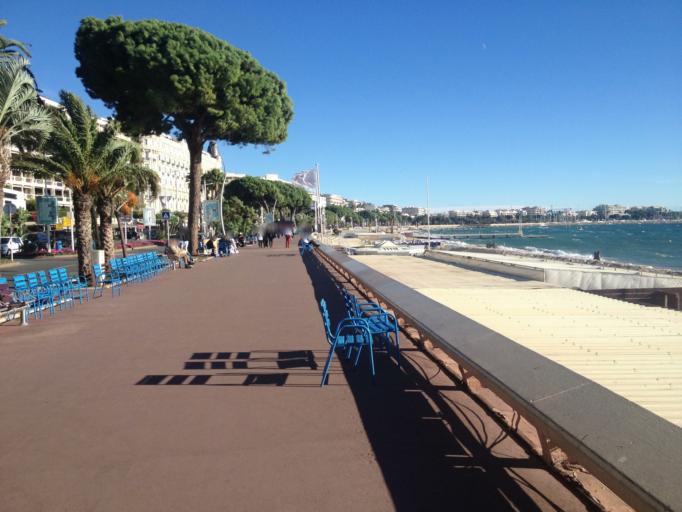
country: FR
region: Provence-Alpes-Cote d'Azur
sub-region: Departement des Alpes-Maritimes
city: Cannes
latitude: 43.5499
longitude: 7.0244
